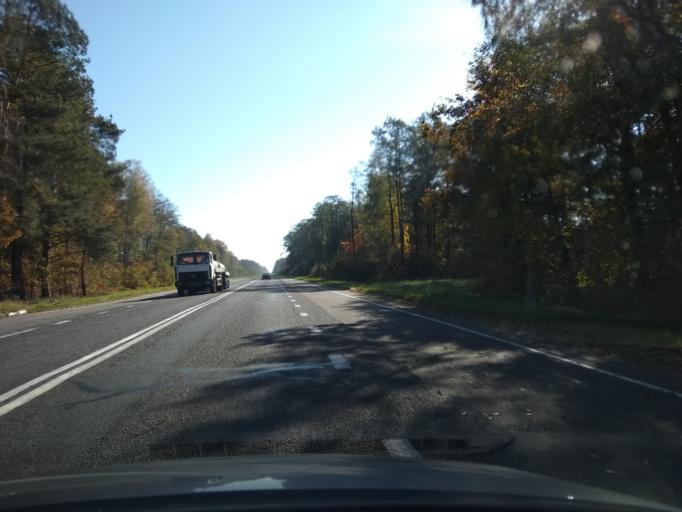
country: BY
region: Brest
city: Malaryta
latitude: 51.9212
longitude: 24.0816
